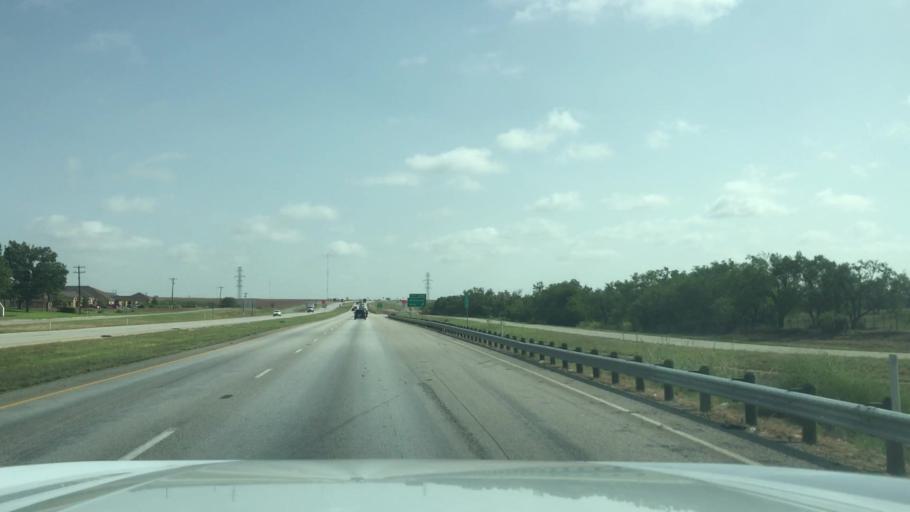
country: US
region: Texas
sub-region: Nolan County
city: Sweetwater
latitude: 32.4593
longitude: -100.3862
